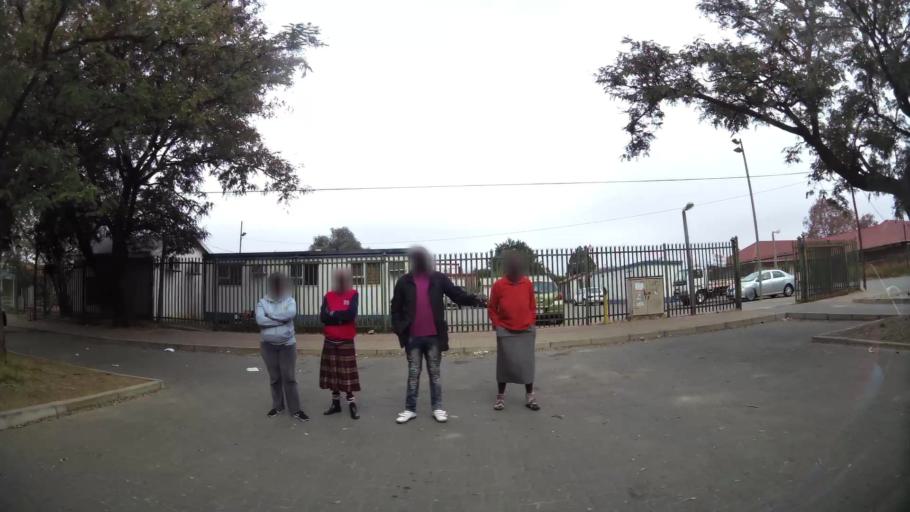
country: ZA
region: Gauteng
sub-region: City of Tshwane Metropolitan Municipality
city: Pretoria
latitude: -25.7138
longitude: 28.3478
